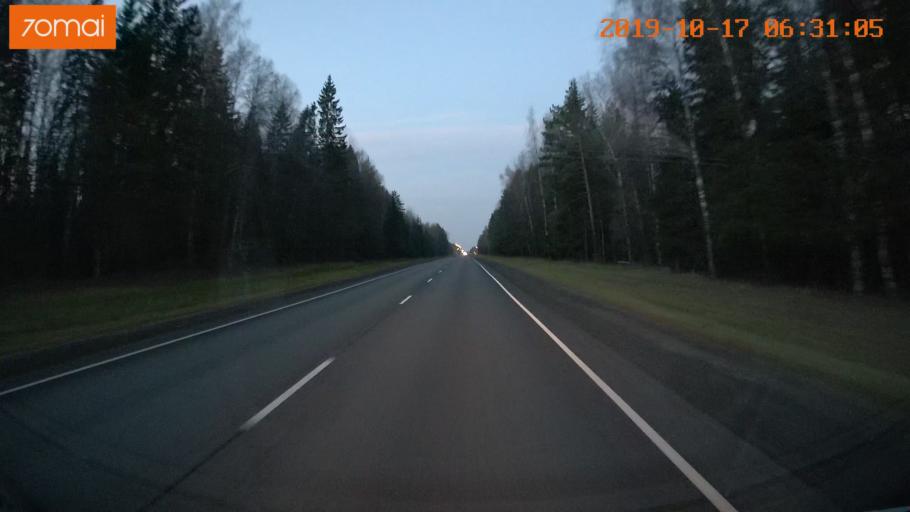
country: RU
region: Ivanovo
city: Lezhnevo
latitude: 56.7307
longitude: 40.7055
